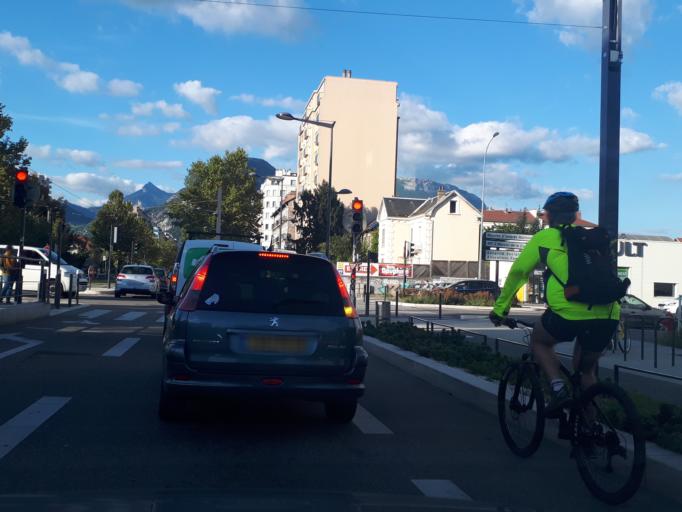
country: FR
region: Rhone-Alpes
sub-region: Departement de l'Isere
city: Grenoble
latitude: 45.1741
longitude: 5.7145
